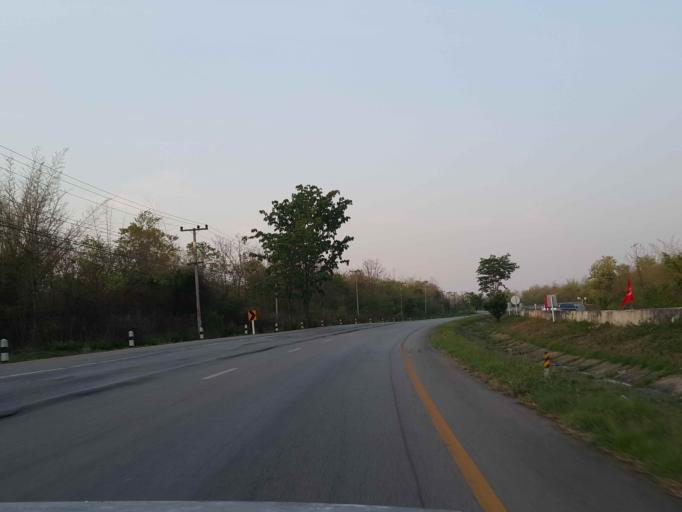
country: TH
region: Lampang
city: Sop Prap
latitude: 17.9704
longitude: 99.3530
